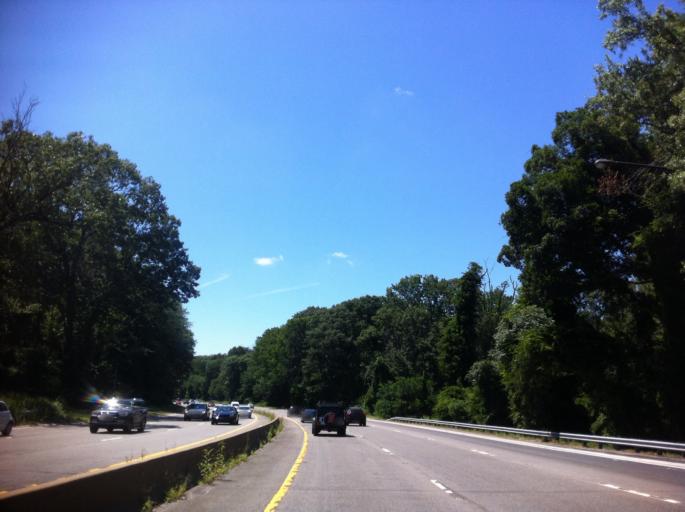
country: US
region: New York
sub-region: Nassau County
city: North Hills
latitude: 40.7736
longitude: -73.6704
